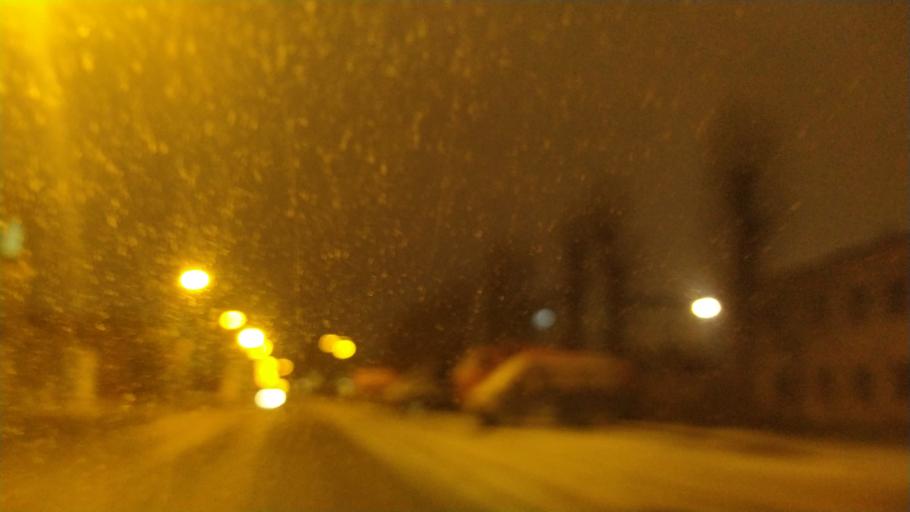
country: RU
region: St.-Petersburg
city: Kupchino
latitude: 59.8824
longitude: 30.3320
